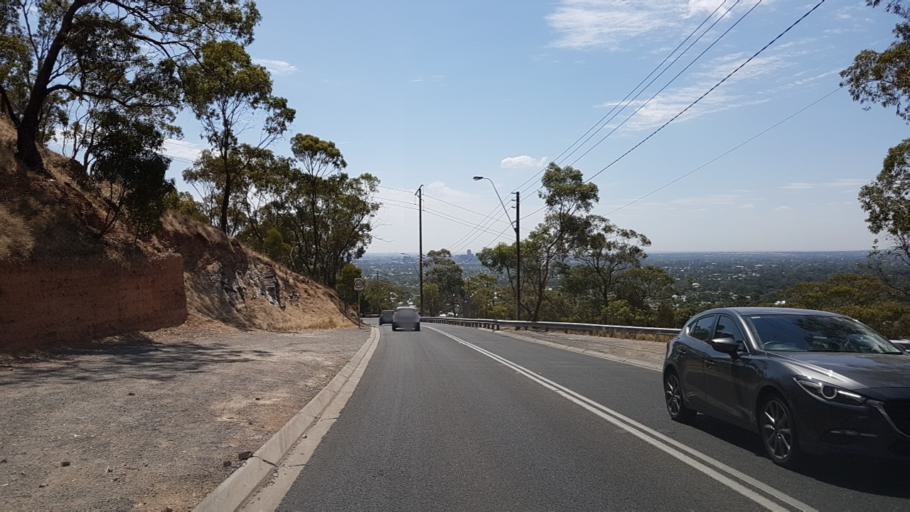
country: AU
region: South Australia
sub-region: Mitcham
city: Mitcham
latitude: -34.9879
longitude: 138.6251
